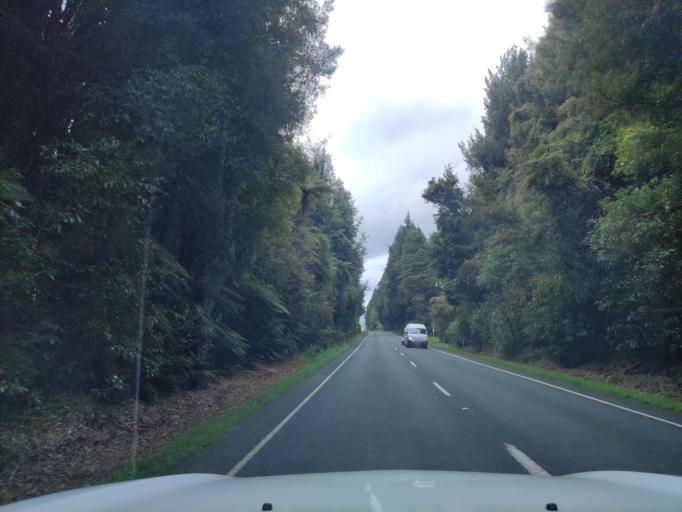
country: NZ
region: Waikato
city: Turangi
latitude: -38.9949
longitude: 175.3783
